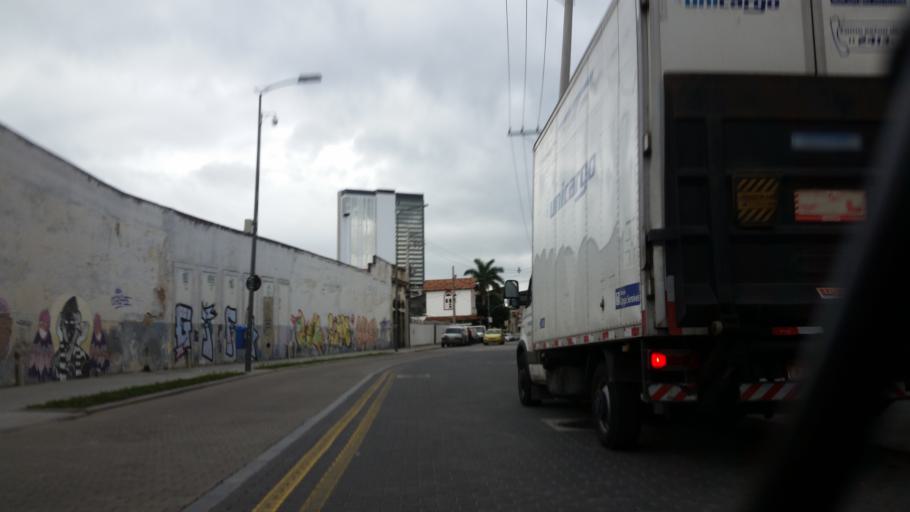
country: BR
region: Rio de Janeiro
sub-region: Rio De Janeiro
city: Rio de Janeiro
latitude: -22.9071
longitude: -43.2085
